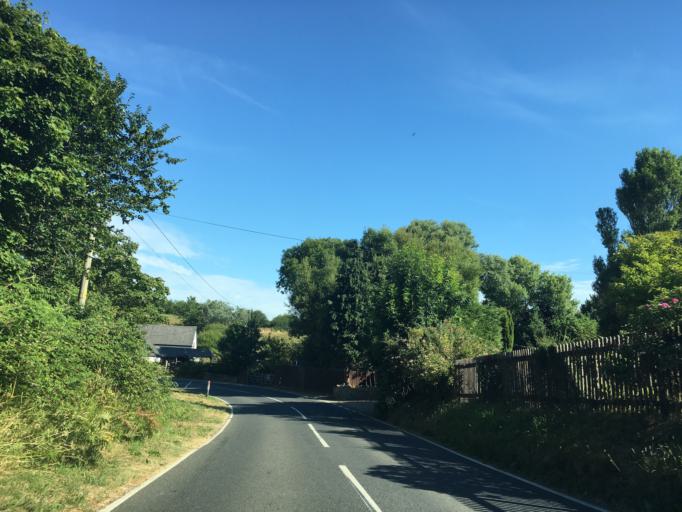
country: GB
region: England
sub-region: Isle of Wight
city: Niton
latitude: 50.6101
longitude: -1.2790
